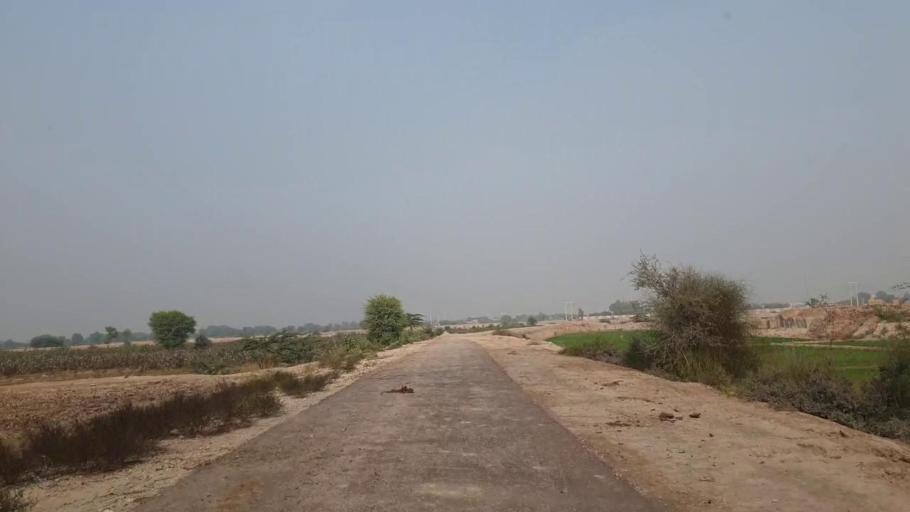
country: PK
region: Sindh
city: Bhan
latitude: 26.5437
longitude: 67.7092
